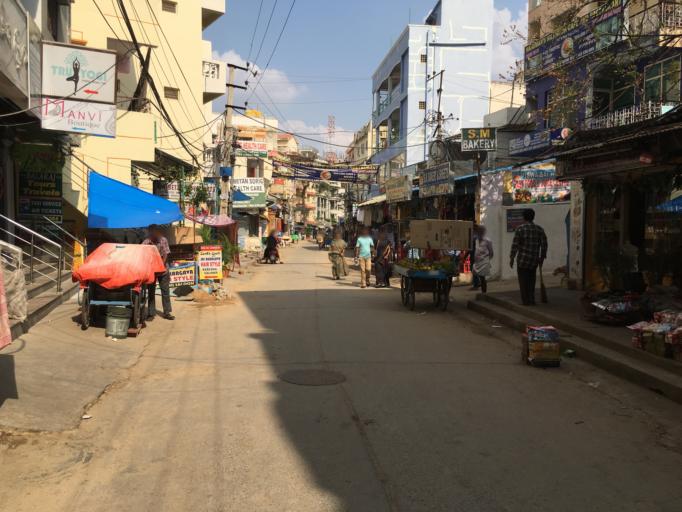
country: IN
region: Andhra Pradesh
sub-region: Anantapur
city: Puttaparthi
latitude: 14.1651
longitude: 77.8125
